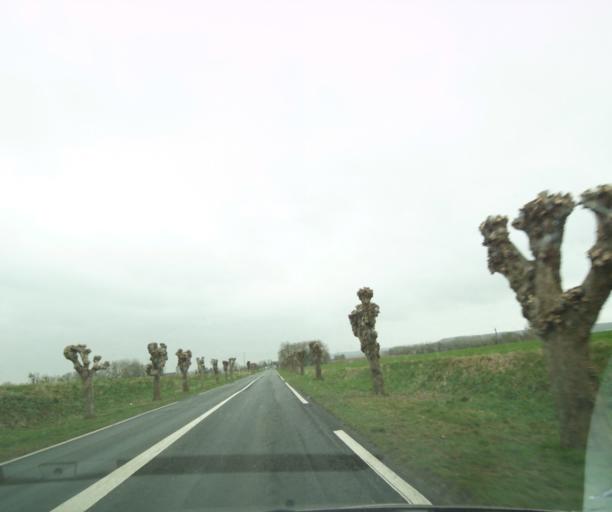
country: FR
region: Picardie
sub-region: Departement de l'Oise
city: Noyon
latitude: 49.5962
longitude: 3.0068
